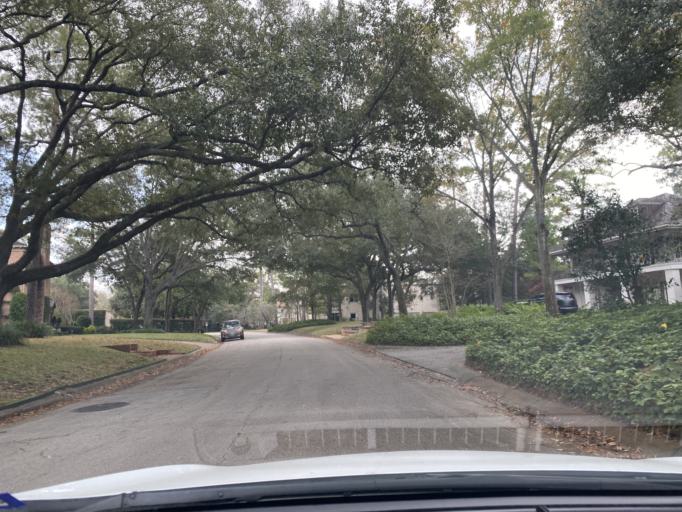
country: US
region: Texas
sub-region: Harris County
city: Hunters Creek Village
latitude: 29.7683
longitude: -95.4696
